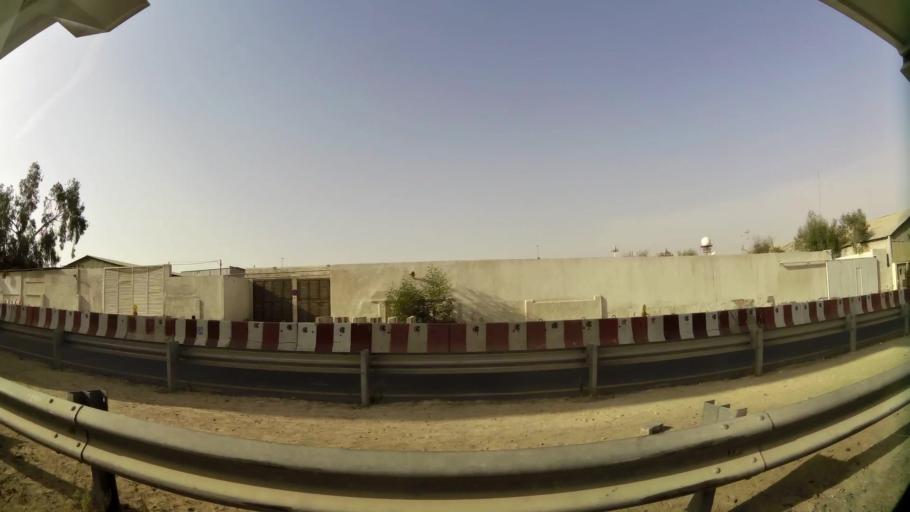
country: AE
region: Ash Shariqah
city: Sharjah
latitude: 25.2370
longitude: 55.3737
